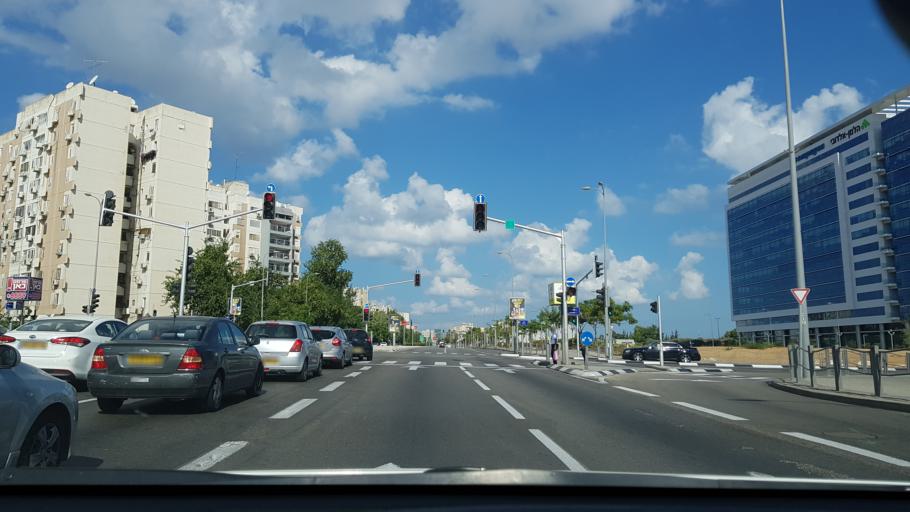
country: IL
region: Tel Aviv
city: Azor
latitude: 32.0054
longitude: 34.7997
